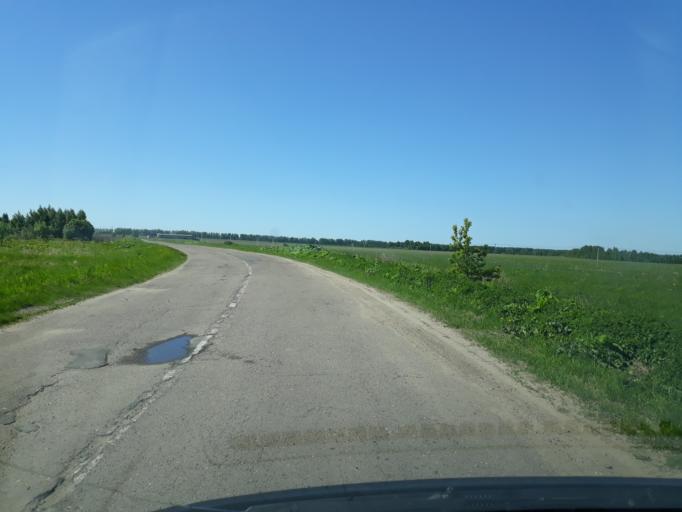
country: RU
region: Jaroslavl
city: Yaroslavl
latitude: 57.6798
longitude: 40.0173
